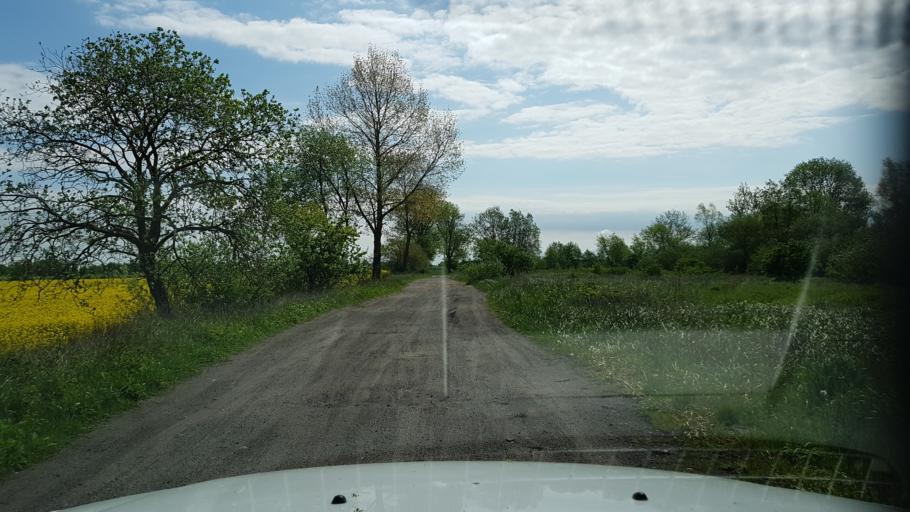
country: PL
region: West Pomeranian Voivodeship
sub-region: Powiat kolobrzeski
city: Ustronie Morskie
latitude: 54.2213
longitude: 15.8252
